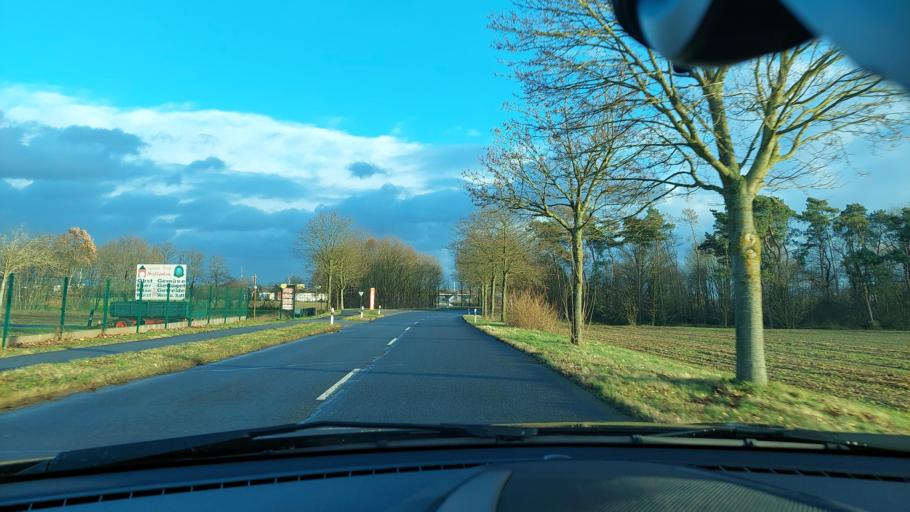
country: DE
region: North Rhine-Westphalia
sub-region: Regierungsbezirk Dusseldorf
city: Dormagen
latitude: 51.0720
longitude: 6.7961
